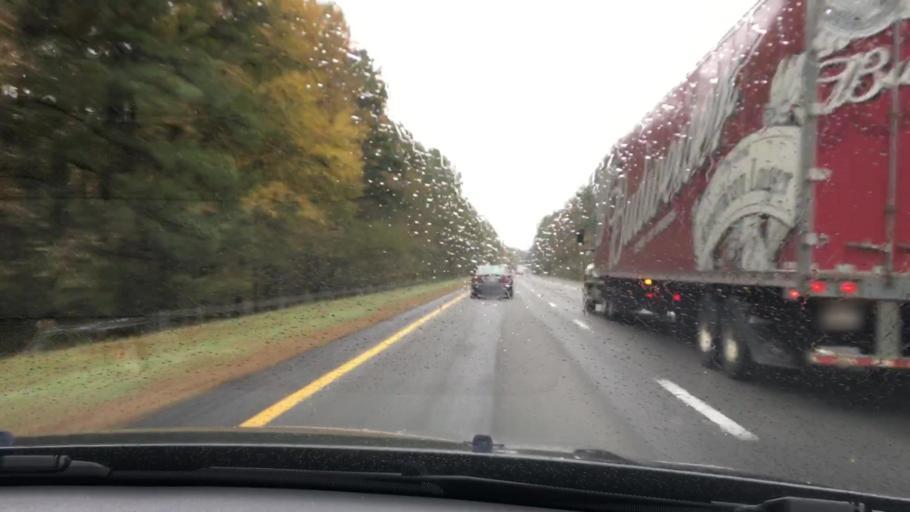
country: US
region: Virginia
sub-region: King William County
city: West Point
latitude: 37.4579
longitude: -76.8801
